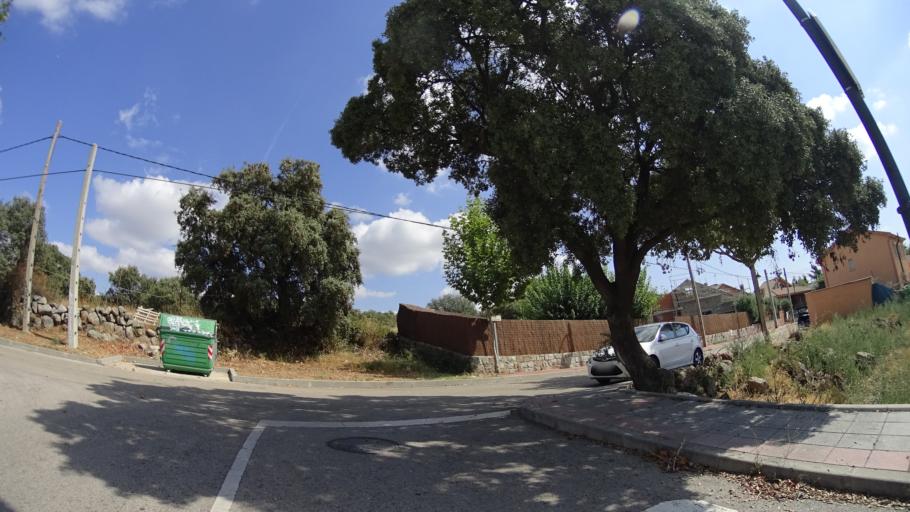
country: ES
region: Madrid
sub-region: Provincia de Madrid
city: Galapagar
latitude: 40.5861
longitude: -3.9961
